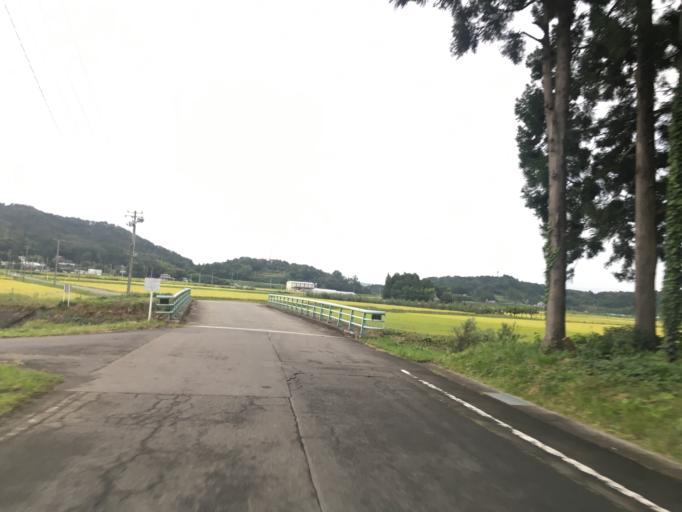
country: JP
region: Fukushima
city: Nihommatsu
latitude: 37.6562
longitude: 140.4445
